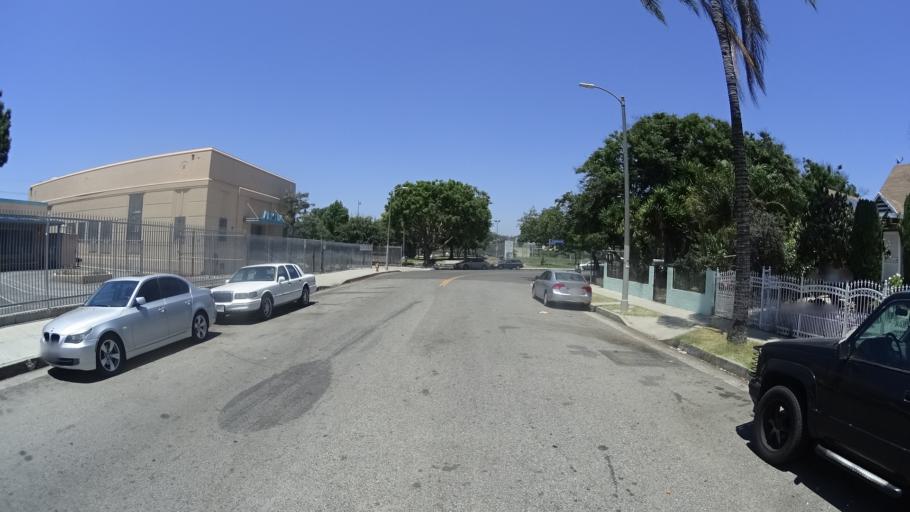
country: US
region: California
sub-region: Los Angeles County
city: View Park-Windsor Hills
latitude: 34.0126
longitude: -118.3080
